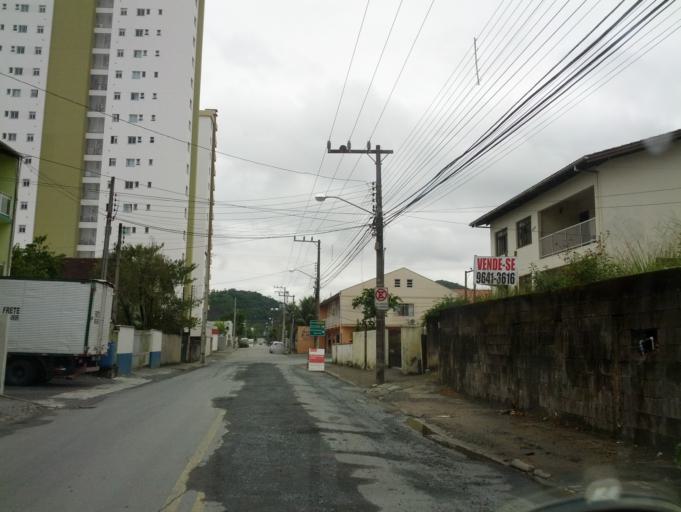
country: BR
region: Santa Catarina
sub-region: Blumenau
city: Blumenau
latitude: -26.8885
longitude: -49.0678
